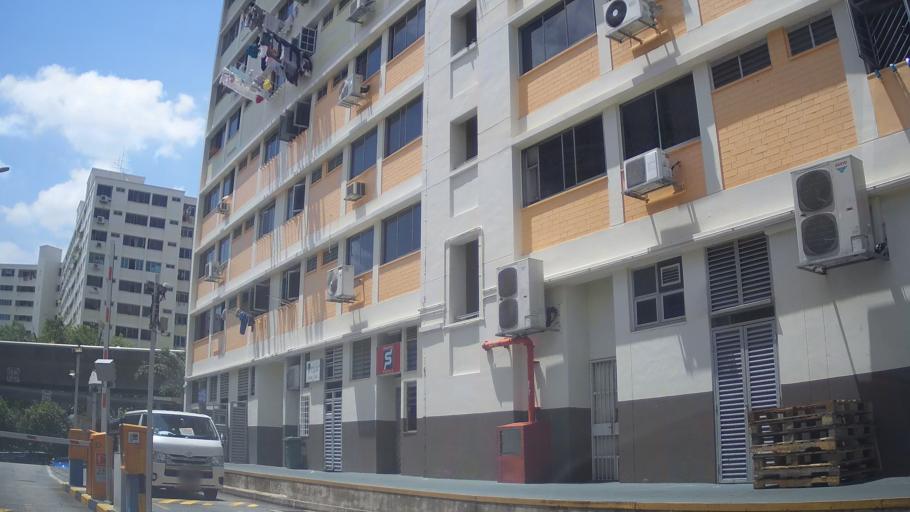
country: MY
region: Johor
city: Johor Bahru
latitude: 1.3783
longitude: 103.7730
